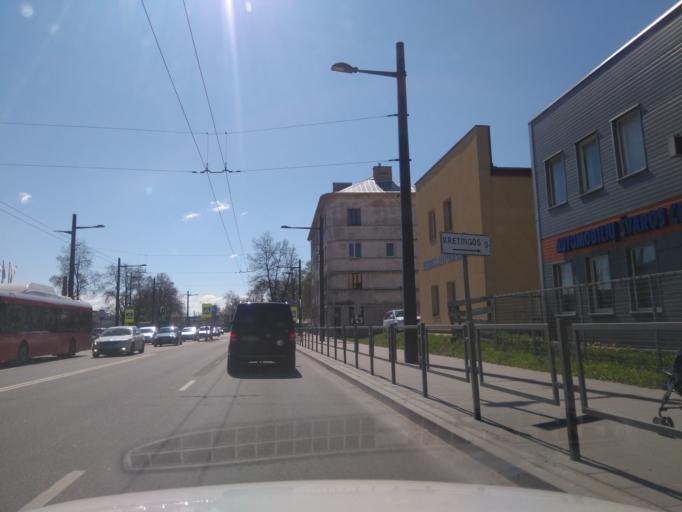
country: LT
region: Kauno apskritis
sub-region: Kaunas
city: Aleksotas
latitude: 54.8775
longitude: 23.9343
